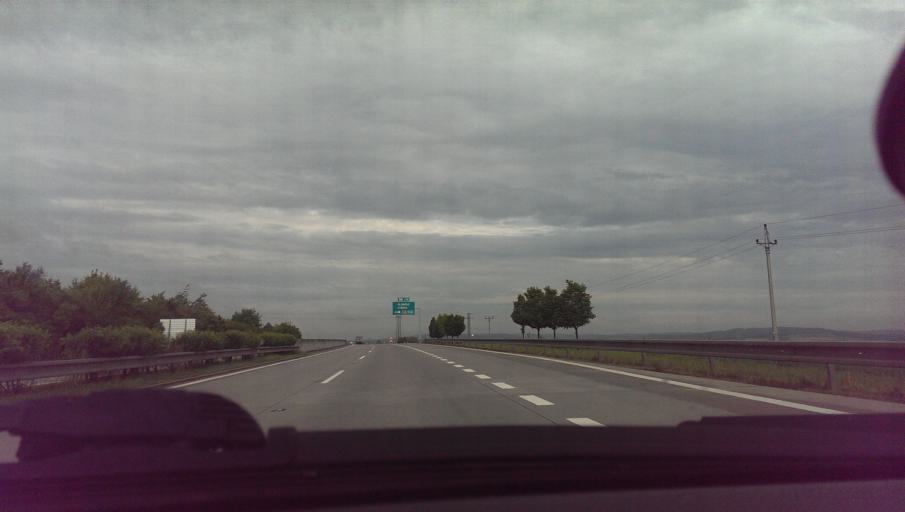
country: CZ
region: South Moravian
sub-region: Okres Vyskov
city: Vyskov
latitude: 49.2729
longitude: 17.0269
